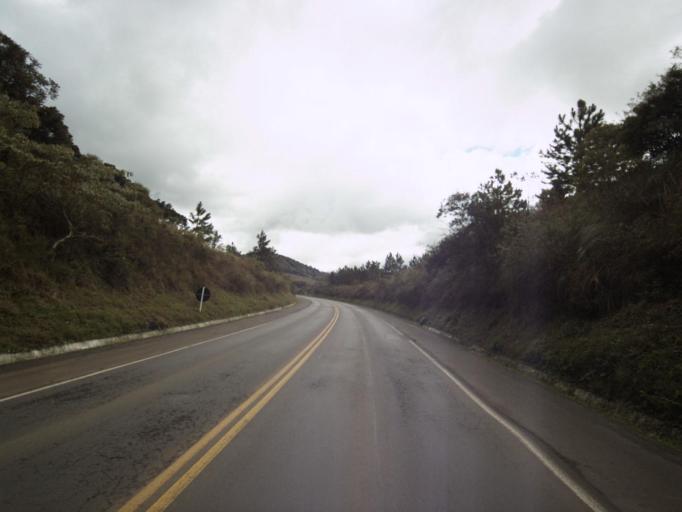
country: BR
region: Santa Catarina
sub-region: Concordia
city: Concordia
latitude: -27.2204
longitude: -51.9488
